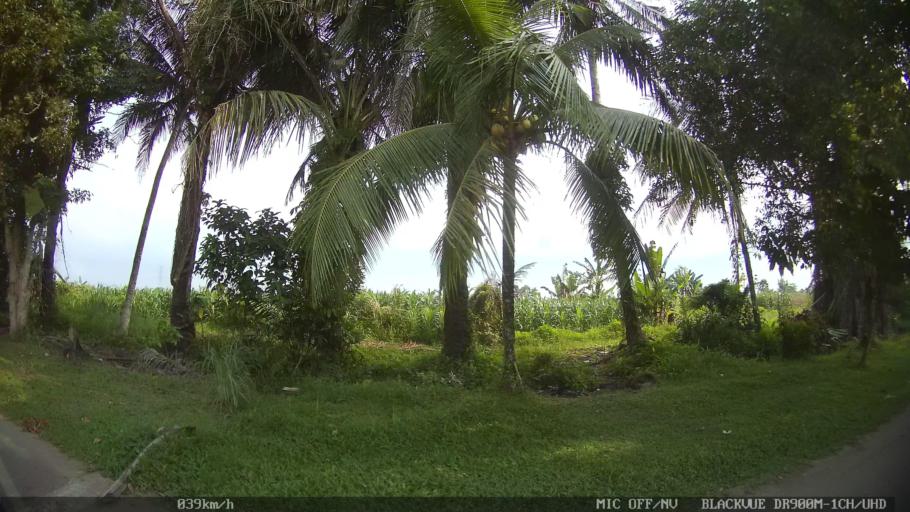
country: ID
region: North Sumatra
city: Binjai
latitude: 3.6029
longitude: 98.5069
